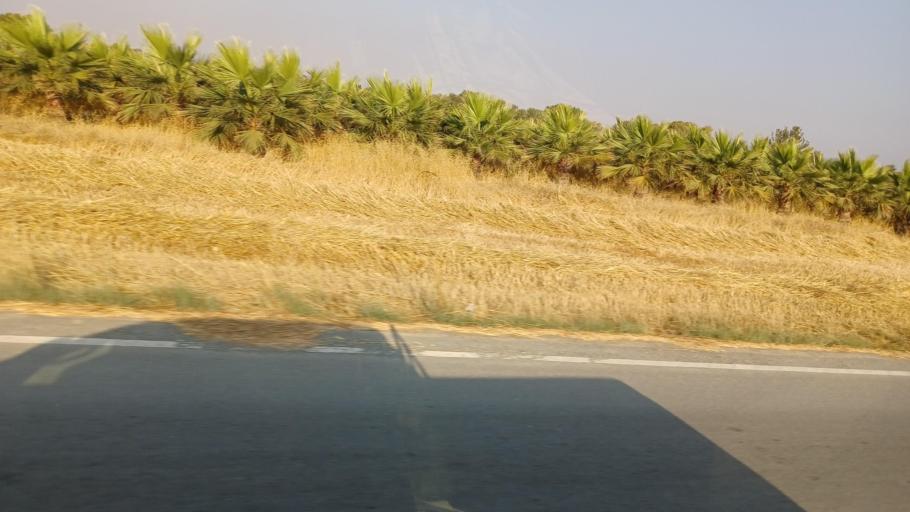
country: CY
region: Larnaka
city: Tersefanou
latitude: 34.8315
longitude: 33.5095
